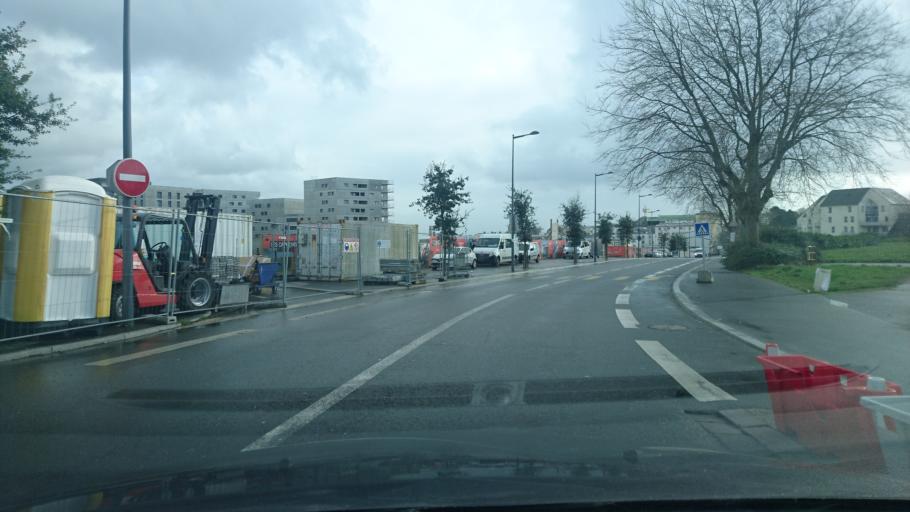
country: FR
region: Brittany
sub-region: Departement du Finistere
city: Brest
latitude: 48.3917
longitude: -4.5038
